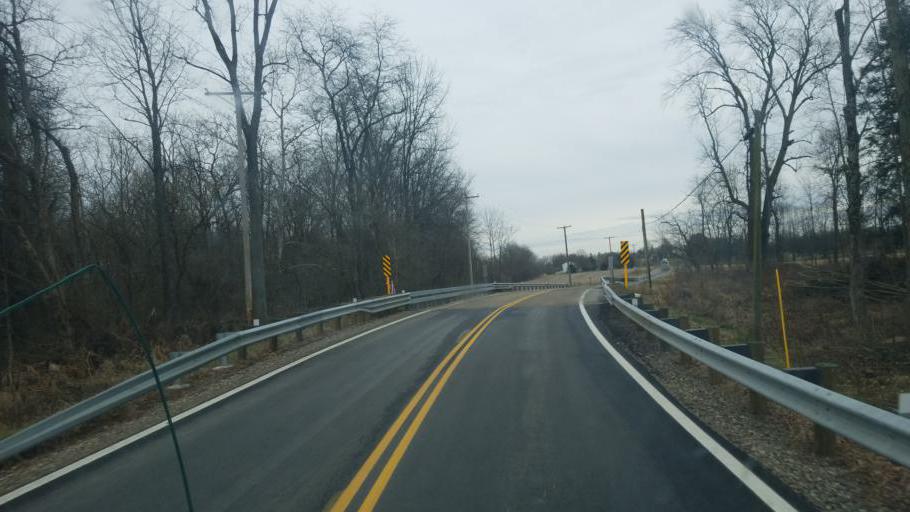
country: US
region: Ohio
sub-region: Knox County
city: Centerburg
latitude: 40.2706
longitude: -82.5993
